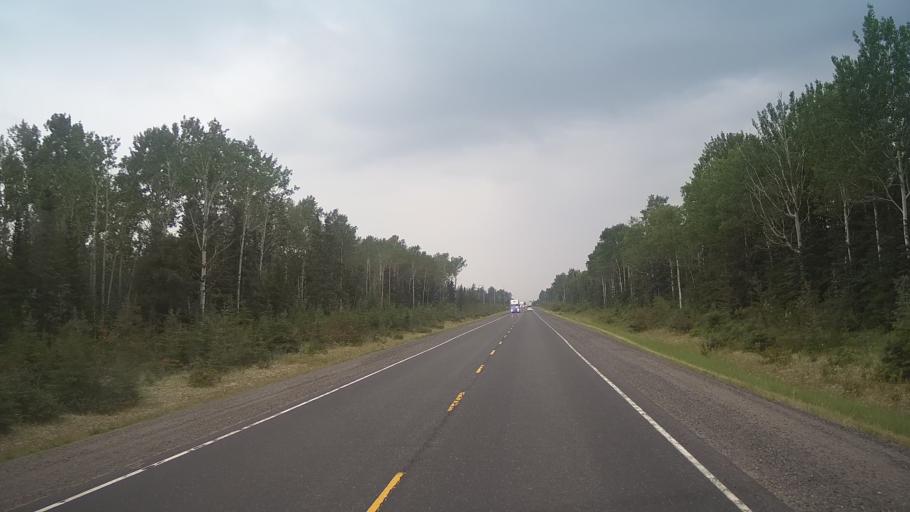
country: CA
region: Ontario
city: Greenstone
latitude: 49.2173
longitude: -88.1982
